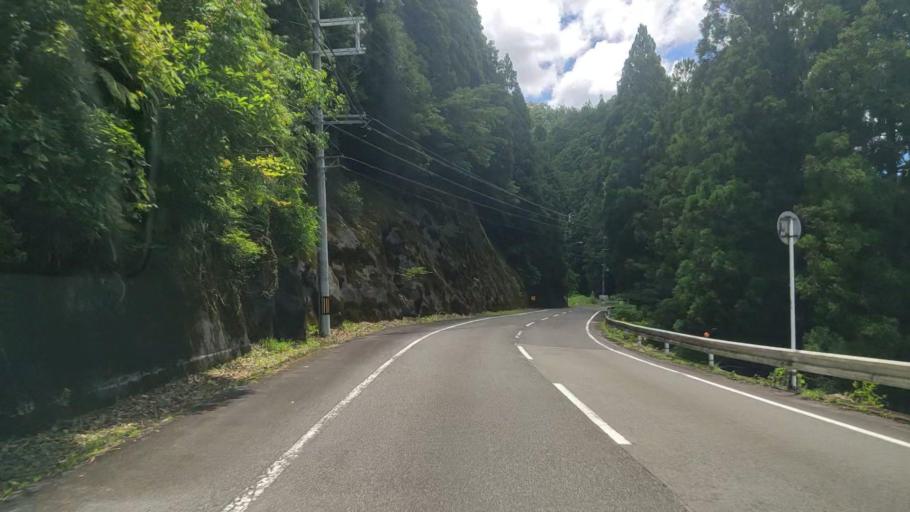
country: JP
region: Mie
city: Owase
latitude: 33.9698
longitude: 136.0614
